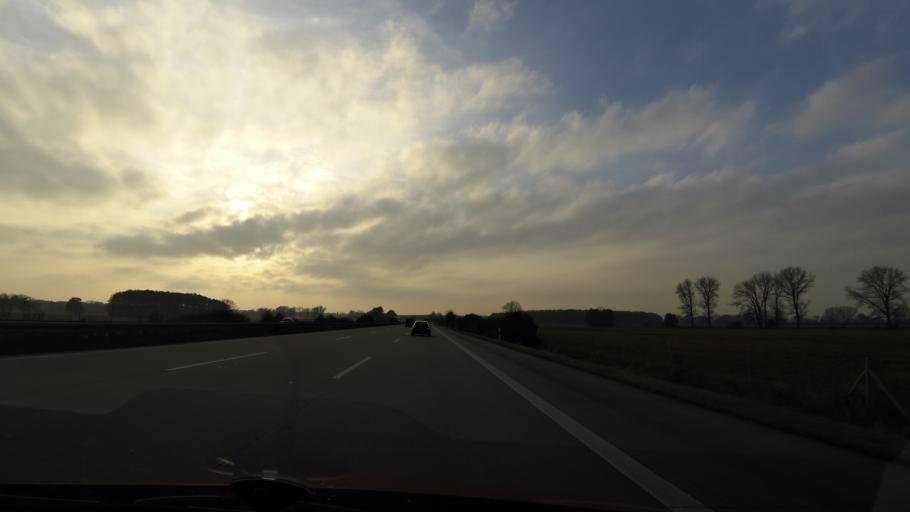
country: DE
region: Brandenburg
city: Linthe
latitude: 52.1682
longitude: 12.8034
